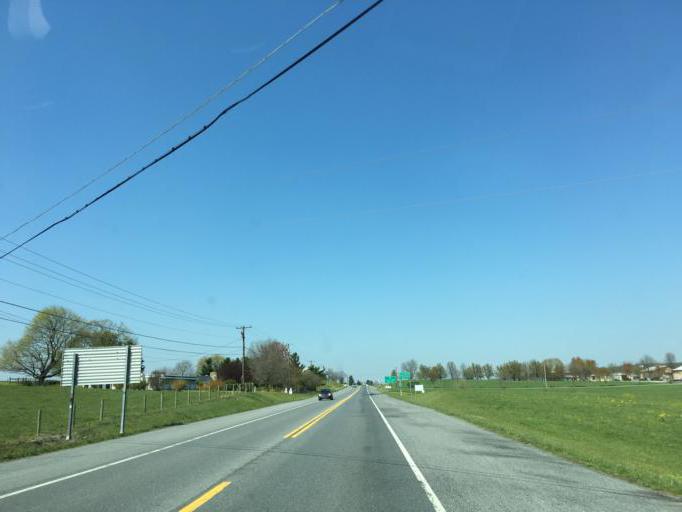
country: US
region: Maryland
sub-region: Frederick County
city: Woodsboro
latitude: 39.5163
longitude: -77.3184
